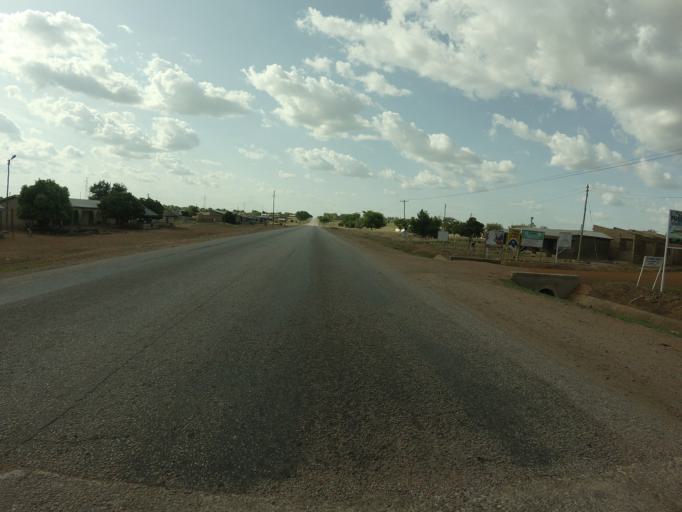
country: GH
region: Upper East
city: Bolgatanga
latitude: 10.6809
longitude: -0.8622
